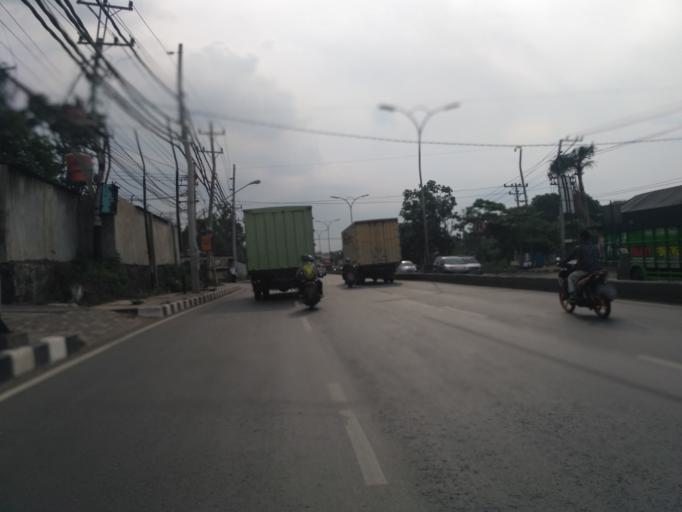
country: ID
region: Central Java
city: Semarang
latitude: -6.9859
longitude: 110.3412
